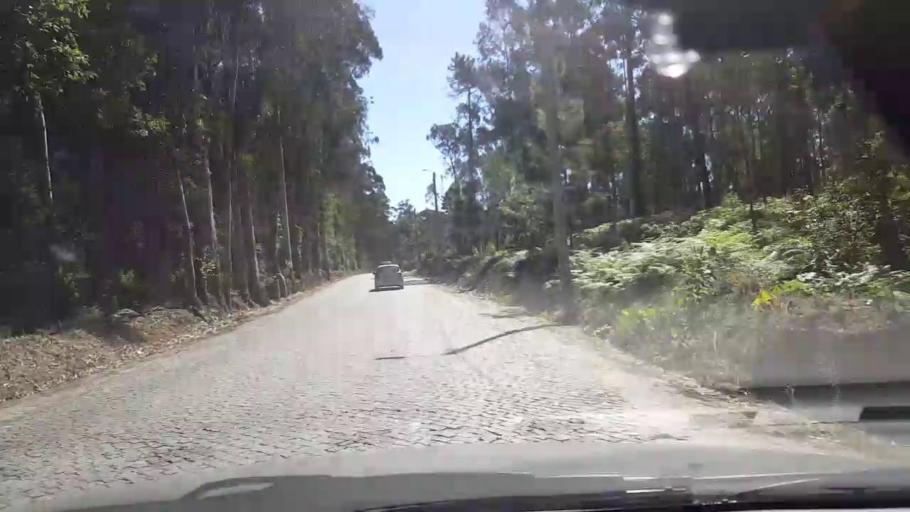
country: PT
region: Porto
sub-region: Vila do Conde
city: Arvore
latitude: 41.3261
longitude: -8.7268
